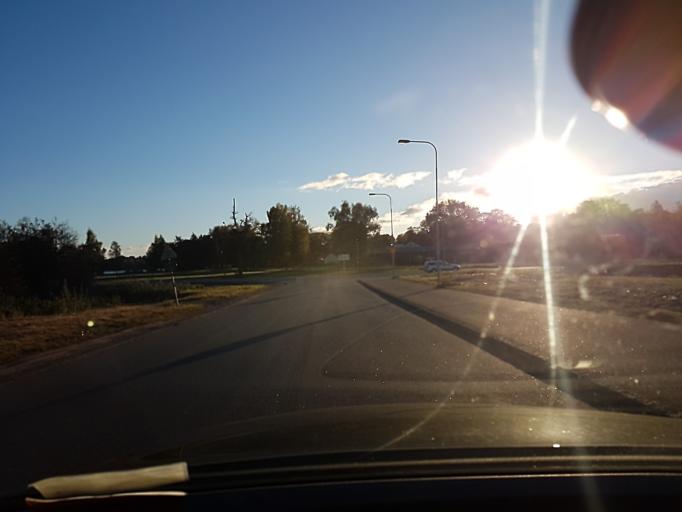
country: SE
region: Kronoberg
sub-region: Vaxjo Kommun
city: Vaexjoe
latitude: 56.8674
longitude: 14.8328
